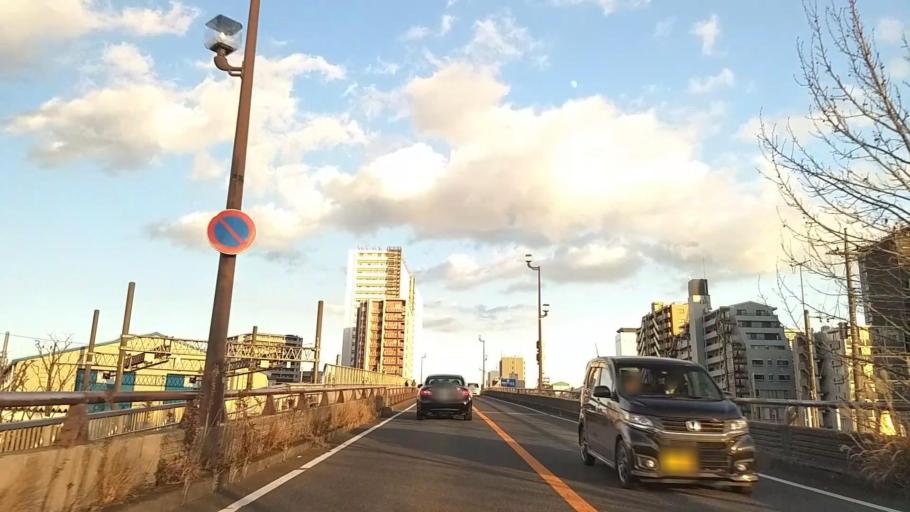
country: JP
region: Kanagawa
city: Atsugi
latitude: 35.4510
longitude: 139.3872
